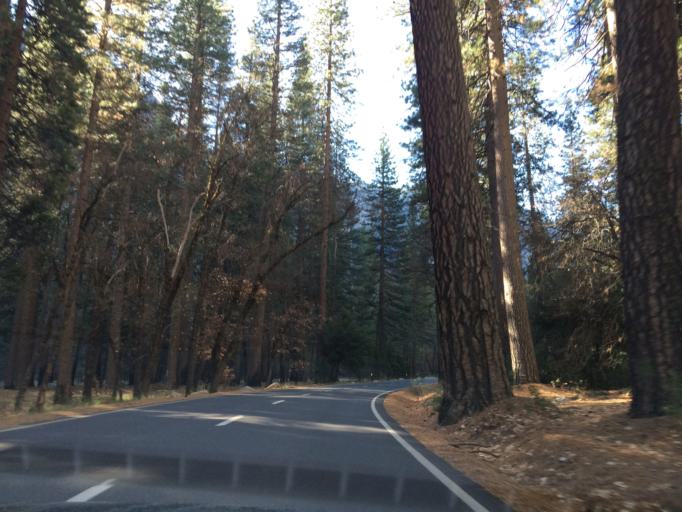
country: US
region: California
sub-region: Mariposa County
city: Yosemite Valley
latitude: 37.7319
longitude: -119.6116
